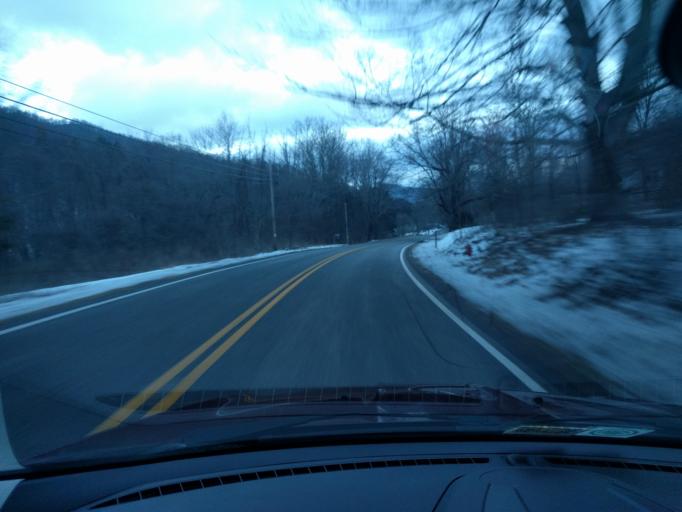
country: US
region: Virginia
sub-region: Alleghany County
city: Clifton Forge
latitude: 37.9382
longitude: -79.8774
